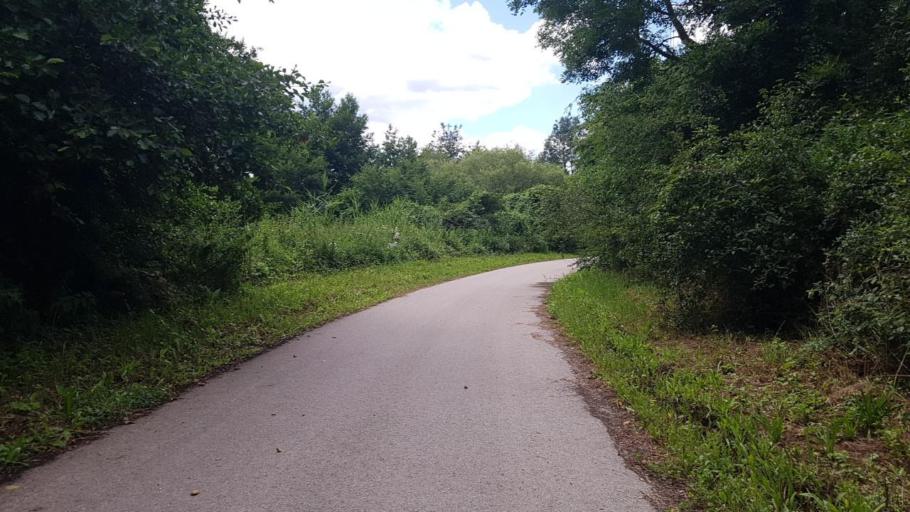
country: FR
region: Champagne-Ardenne
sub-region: Departement de la Marne
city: Mareuil-le-Port
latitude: 49.0824
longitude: 3.7895
